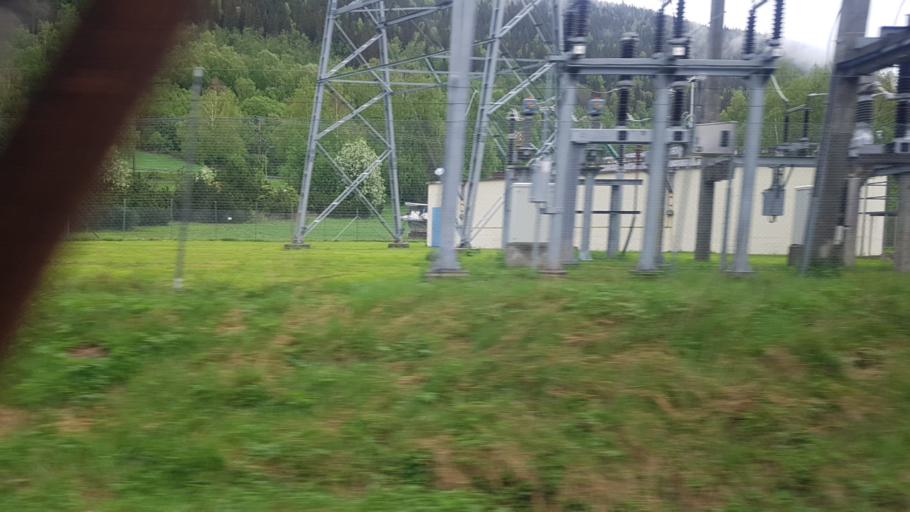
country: NO
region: Oppland
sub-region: Sor-Fron
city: Hundorp
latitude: 61.5737
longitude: 9.8528
